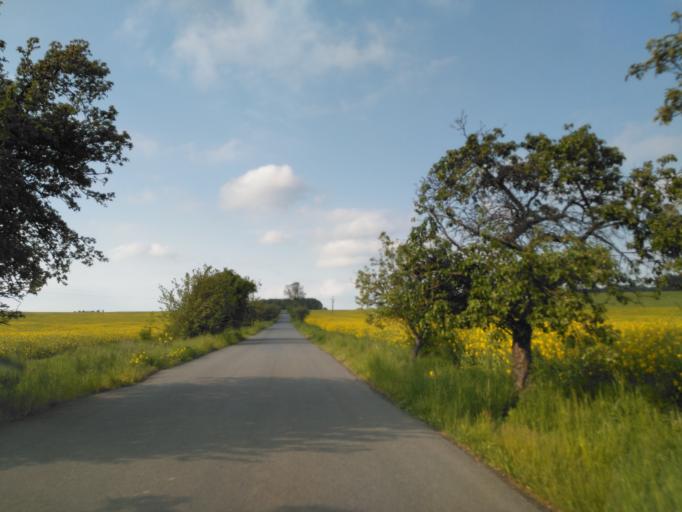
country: CZ
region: Plzensky
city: Zbiroh
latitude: 49.8731
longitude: 13.7968
